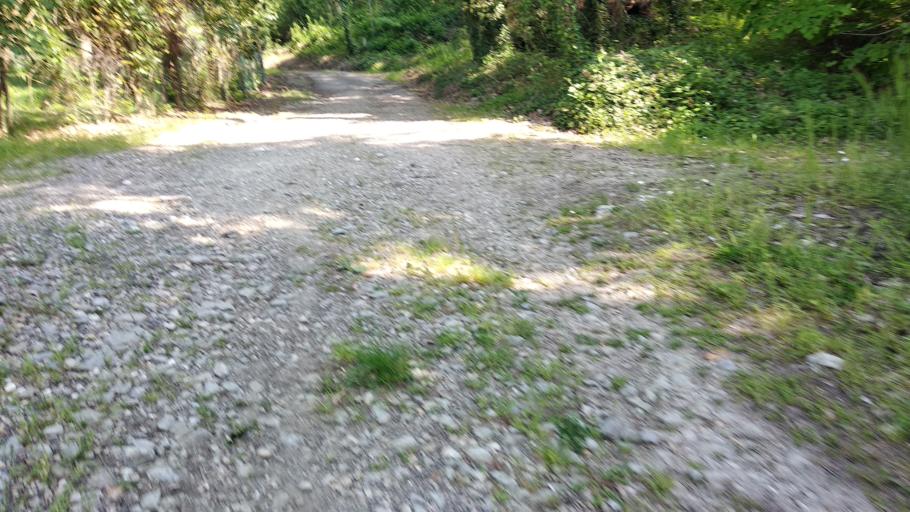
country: IT
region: Emilia-Romagna
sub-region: Provincia di Ravenna
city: Fognano
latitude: 44.2305
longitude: 11.7194
